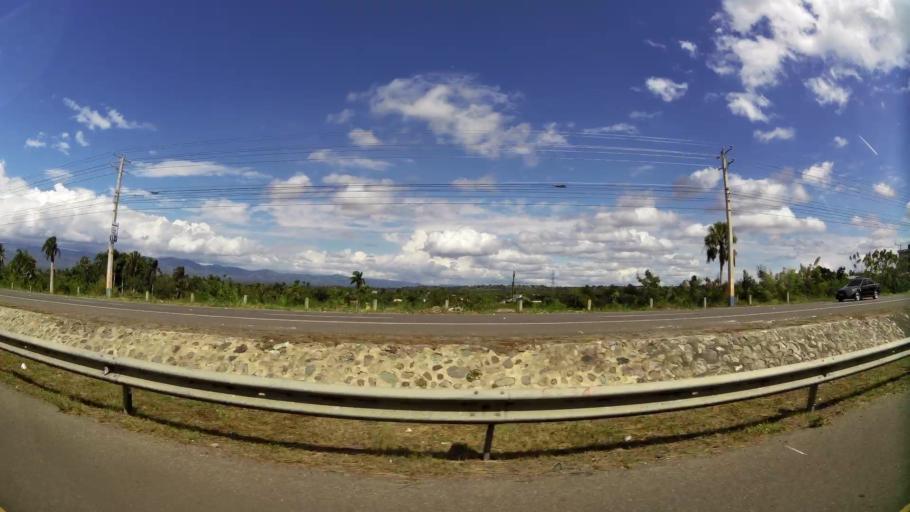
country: DO
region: Santiago
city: Licey al Medio
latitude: 19.3713
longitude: -70.6041
